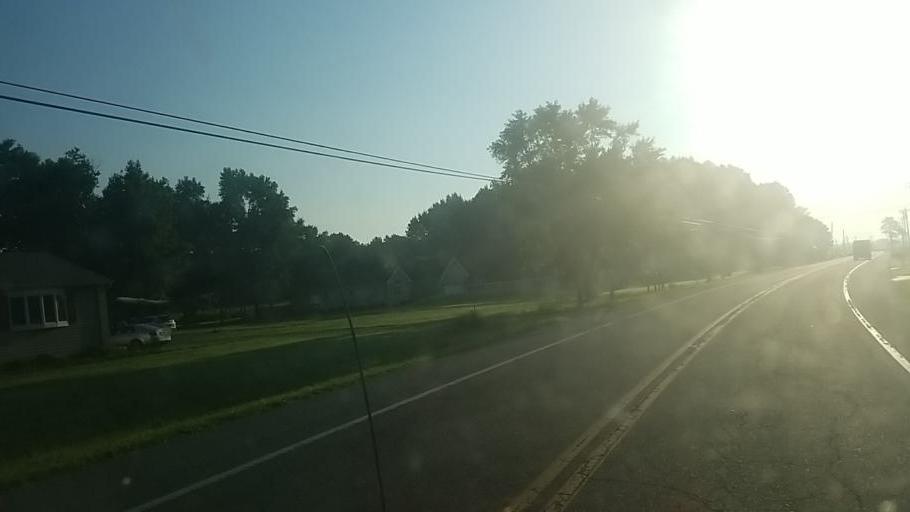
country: US
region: Delaware
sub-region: Sussex County
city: Selbyville
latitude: 38.4624
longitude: -75.1892
